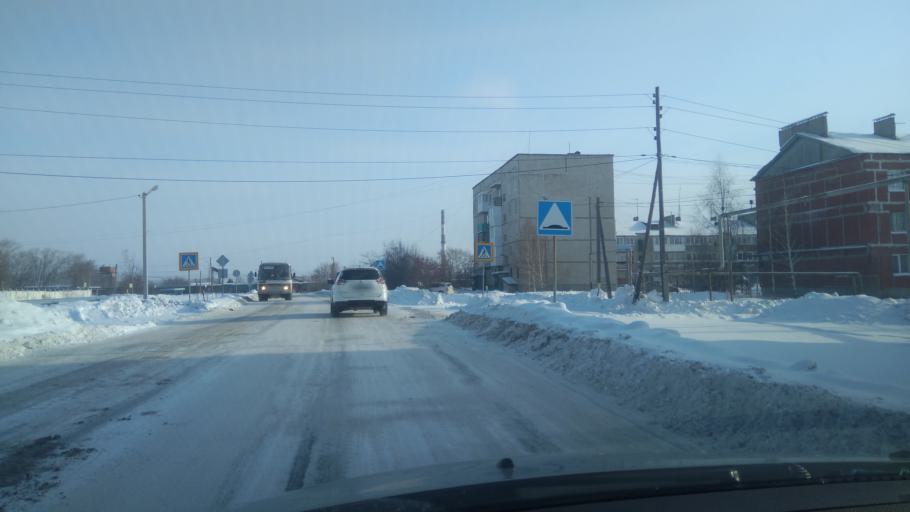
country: RU
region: Sverdlovsk
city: Sukhoy Log
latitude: 56.8910
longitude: 62.0392
